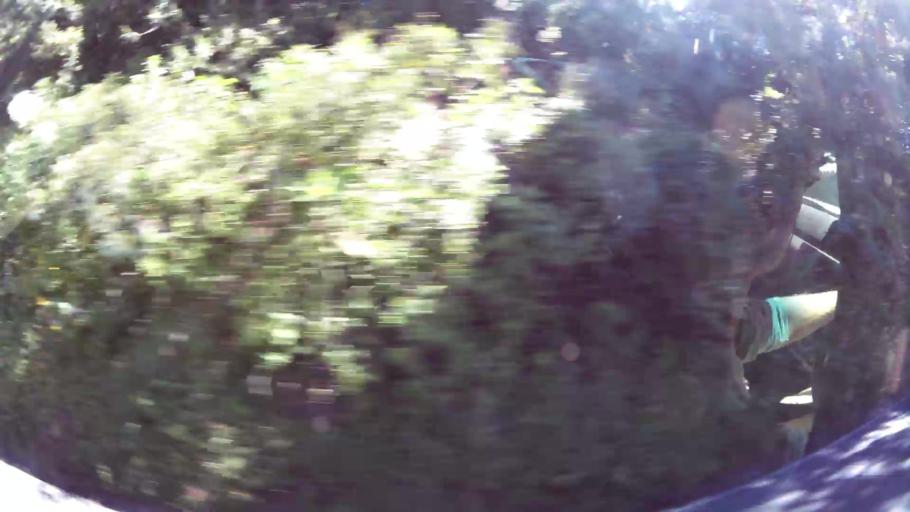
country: GT
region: Solola
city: Solola
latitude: 14.7530
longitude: -91.1706
